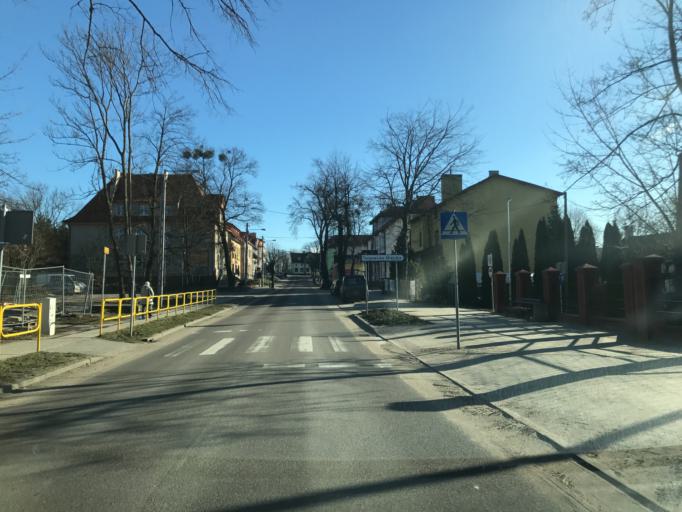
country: PL
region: Warmian-Masurian Voivodeship
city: Dobre Miasto
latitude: 53.9879
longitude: 20.3925
